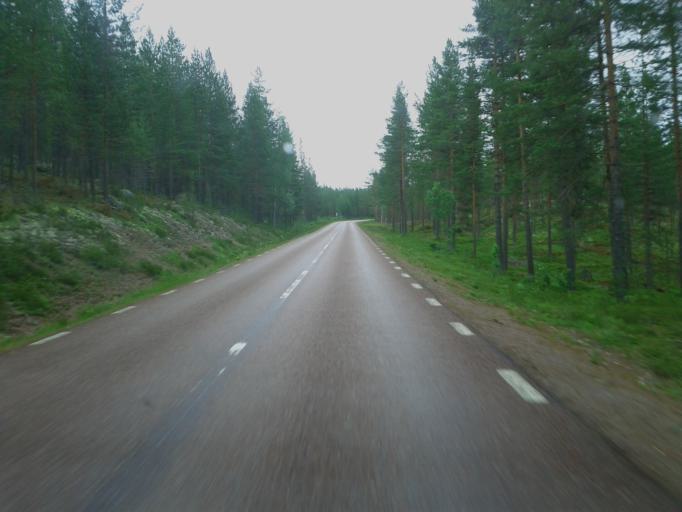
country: NO
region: Hedmark
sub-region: Trysil
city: Innbygda
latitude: 61.7907
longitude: 12.9265
